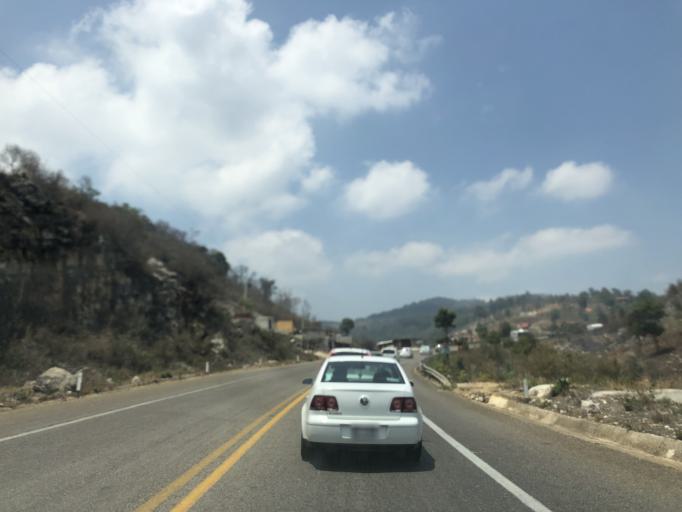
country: MX
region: Chiapas
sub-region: Zinacantan
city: Nachig
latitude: 16.6944
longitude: -92.7085
